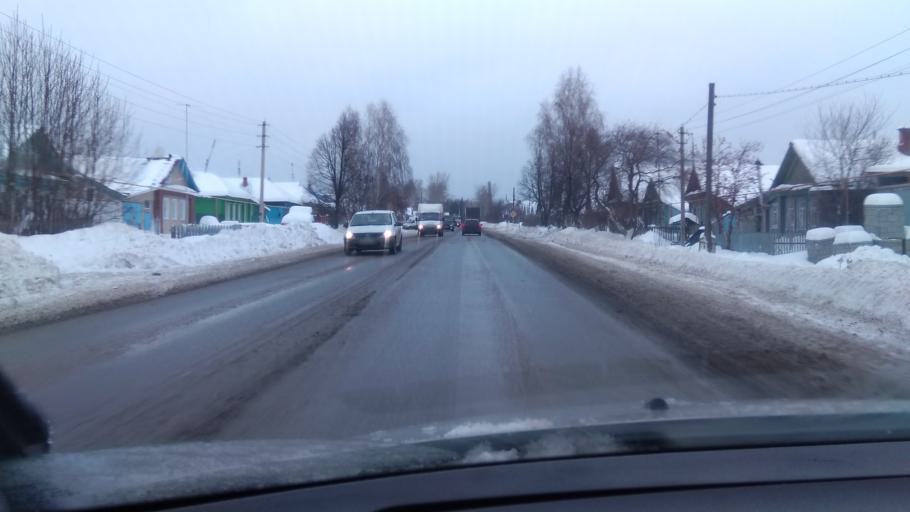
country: RU
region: Sverdlovsk
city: Nikolo-Pavlovskoye
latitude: 57.7904
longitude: 60.0557
